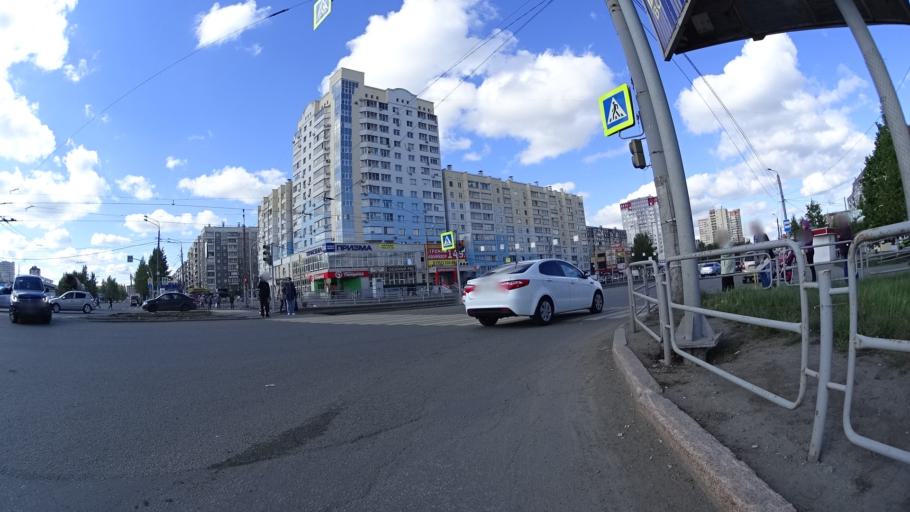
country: RU
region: Chelyabinsk
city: Roshchino
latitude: 55.1826
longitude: 61.2927
